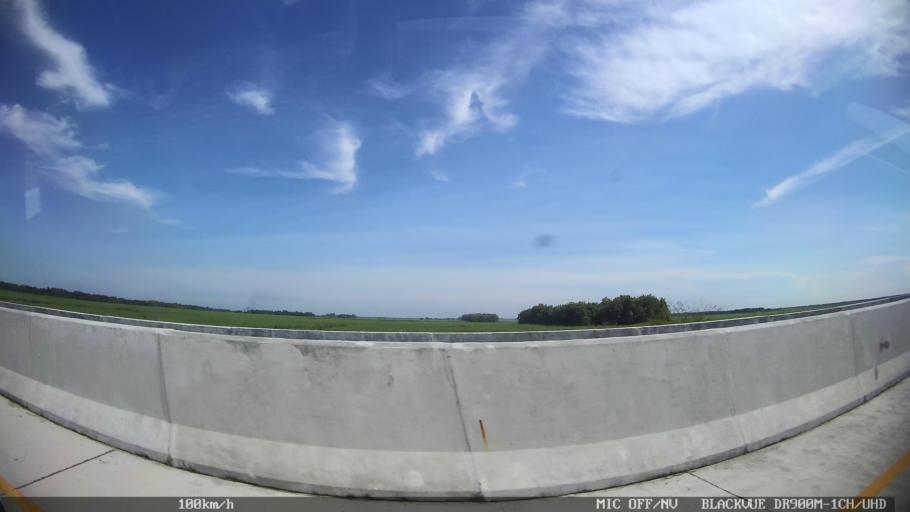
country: ID
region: North Sumatra
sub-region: Kabupaten Langkat
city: Stabat
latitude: 3.7134
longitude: 98.5171
